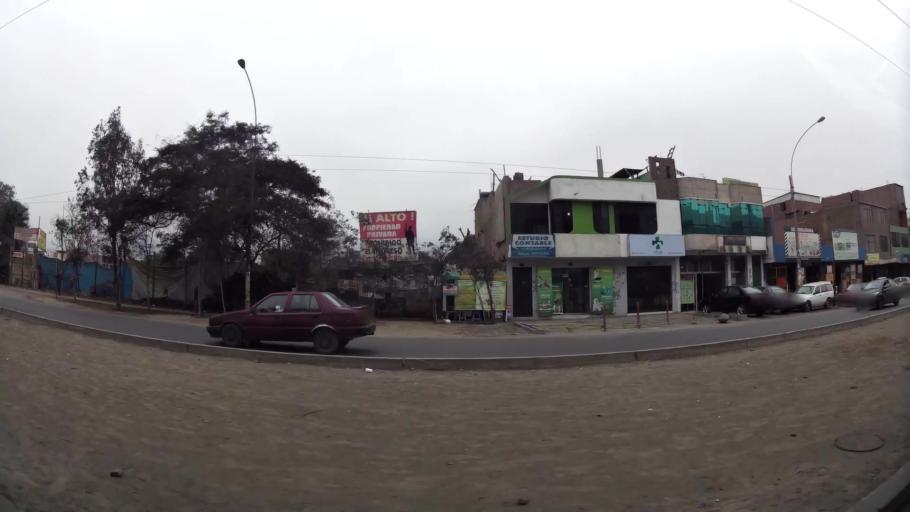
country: PE
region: Lima
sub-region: Lima
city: Independencia
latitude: -11.9791
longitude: -77.0043
